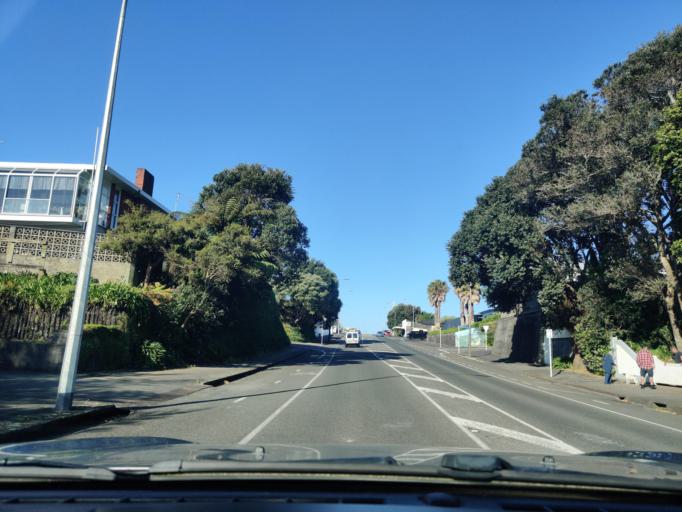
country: NZ
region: Taranaki
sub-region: New Plymouth District
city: New Plymouth
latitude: -39.0524
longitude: 174.0919
